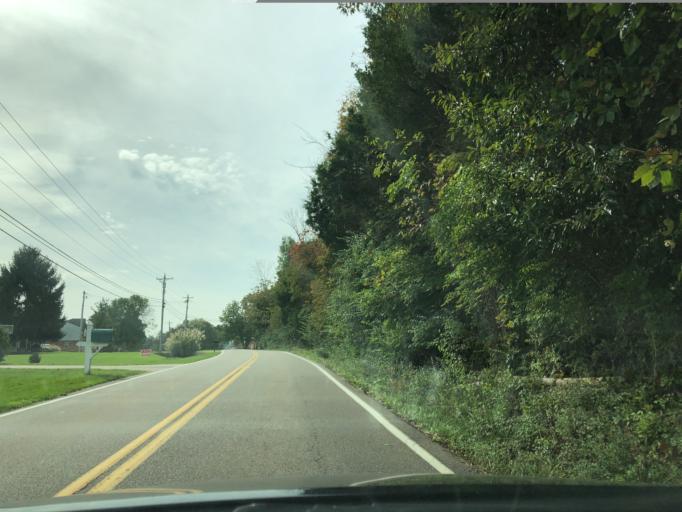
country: US
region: Ohio
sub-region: Hamilton County
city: The Village of Indian Hill
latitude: 39.2307
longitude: -84.2999
